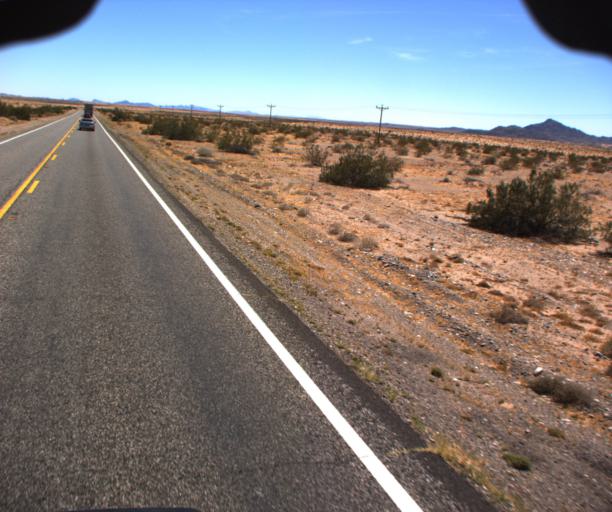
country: US
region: Arizona
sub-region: La Paz County
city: Parker
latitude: 34.0813
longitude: -114.2680
